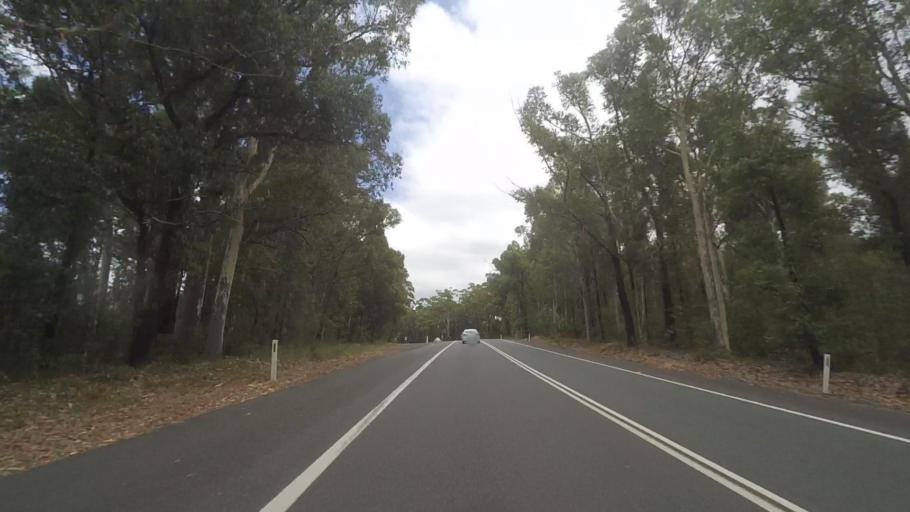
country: AU
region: New South Wales
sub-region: Shoalhaven Shire
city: Milton
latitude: -35.1450
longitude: 150.4620
